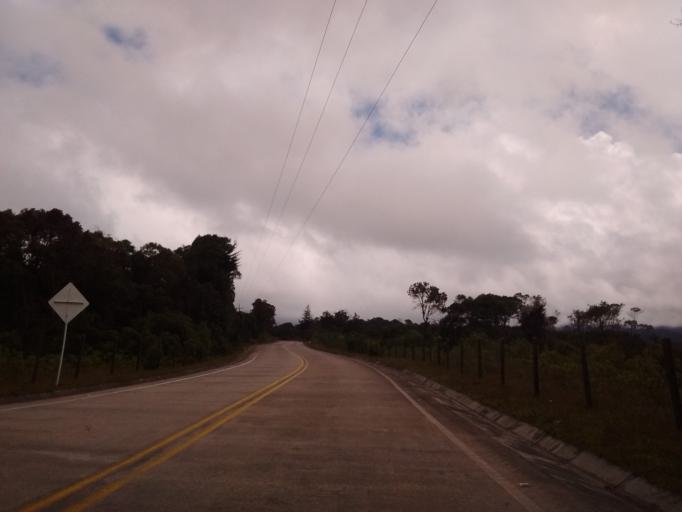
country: CO
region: Huila
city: Isnos
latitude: 2.0525
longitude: -76.3199
